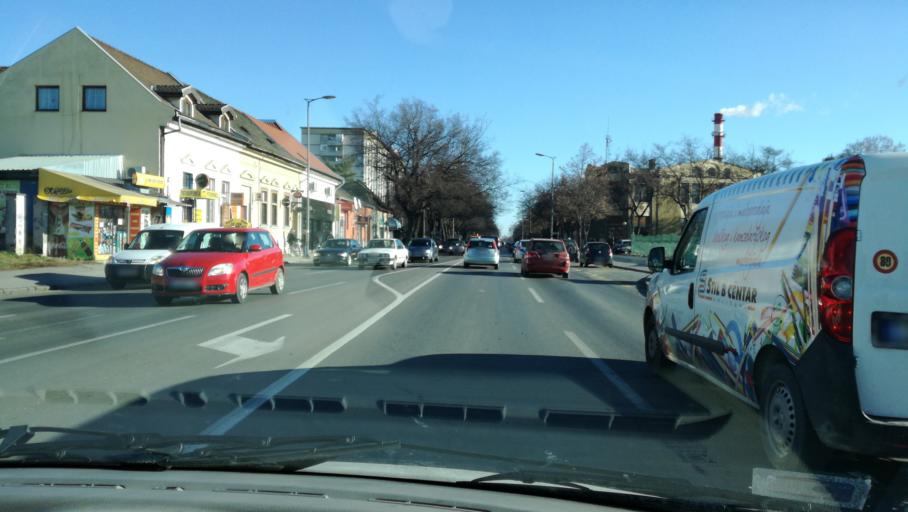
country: RS
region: Autonomna Pokrajina Vojvodina
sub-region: Severnobacki Okrug
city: Subotica
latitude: 46.1001
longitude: 19.6746
